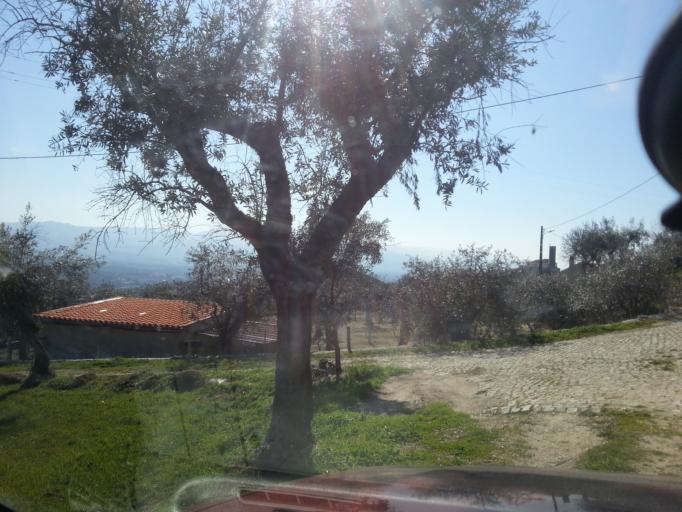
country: PT
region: Guarda
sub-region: Fornos de Algodres
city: Fornos de Algodres
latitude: 40.6248
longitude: -7.5375
